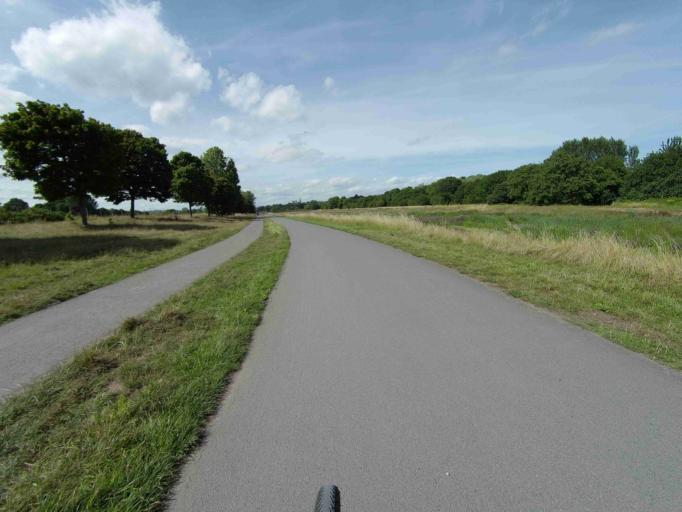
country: GB
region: England
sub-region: Devon
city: Exeter
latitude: 50.7069
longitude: -3.5185
